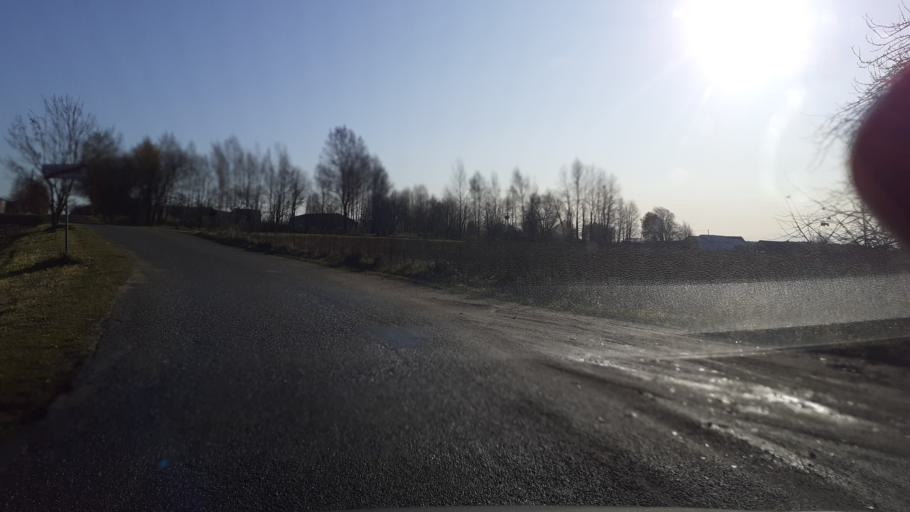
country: LV
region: Kuldigas Rajons
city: Kuldiga
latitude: 56.9979
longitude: 21.8911
